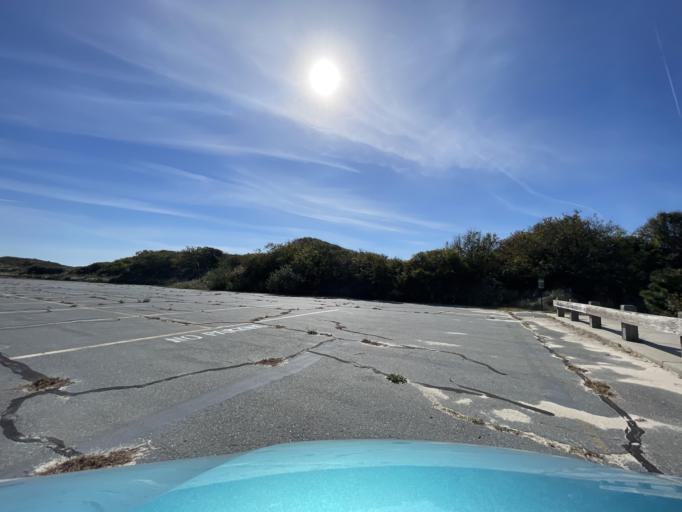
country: US
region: Massachusetts
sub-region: Bristol County
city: Head of Westport
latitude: 41.5055
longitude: -71.0506
